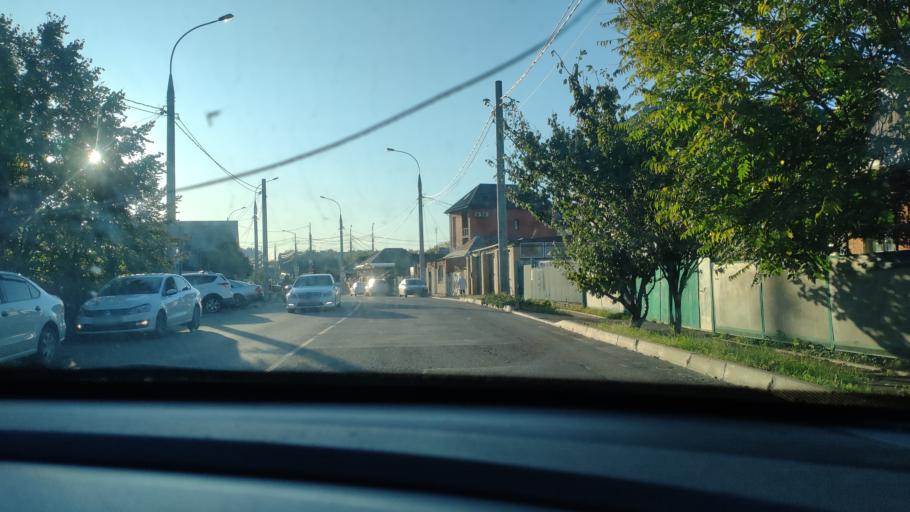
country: RU
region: Krasnodarskiy
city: Krasnodar
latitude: 45.0417
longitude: 38.9313
